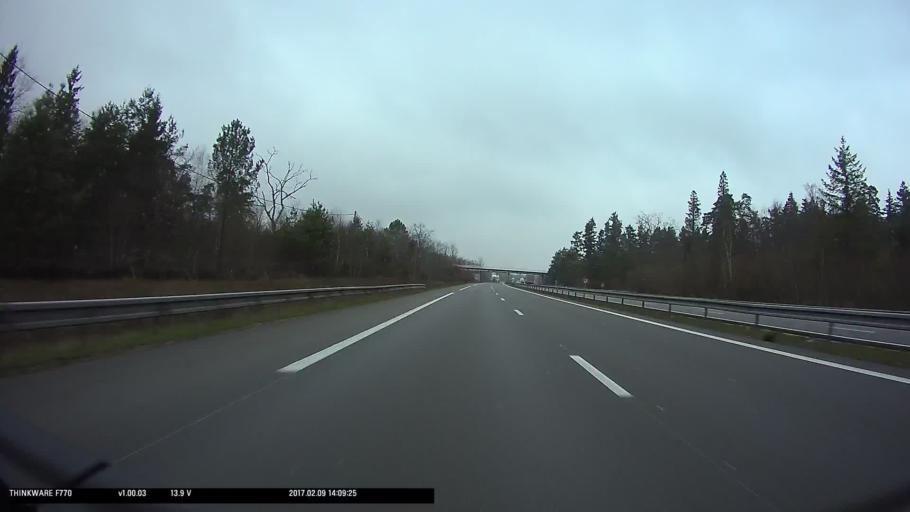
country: FR
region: Centre
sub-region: Departement du Loir-et-Cher
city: Salbris
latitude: 47.4479
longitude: 2.0052
